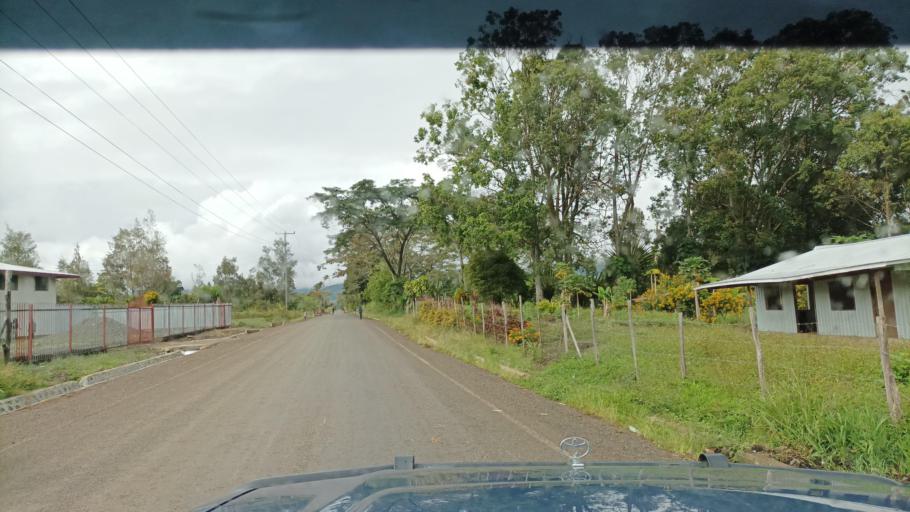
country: PG
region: Jiwaka
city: Minj
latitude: -5.8821
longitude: 144.6805
